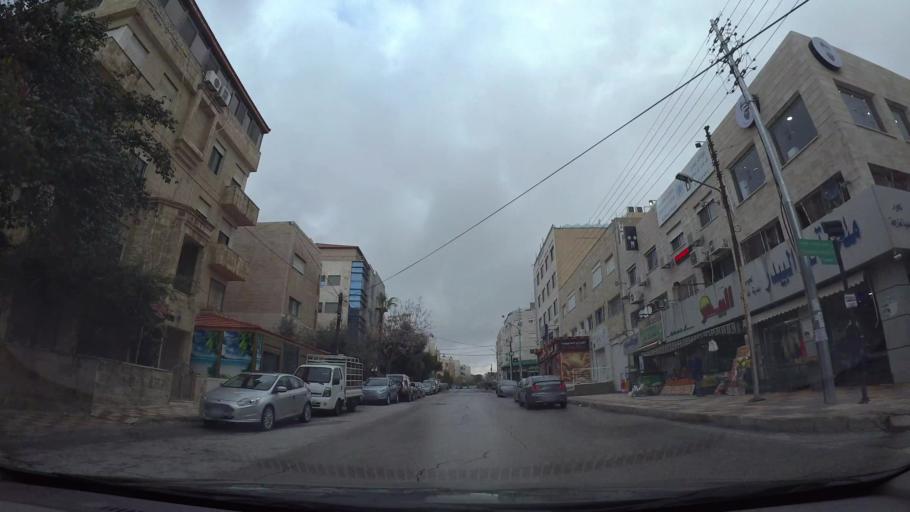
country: JO
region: Amman
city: Wadi as Sir
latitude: 31.9498
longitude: 35.8716
